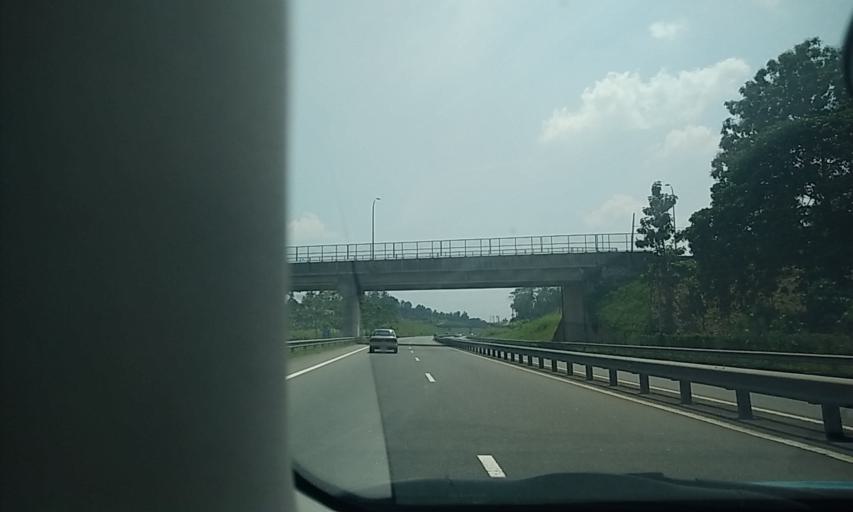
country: LK
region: Western
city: Horana South
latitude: 6.7536
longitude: 79.9942
